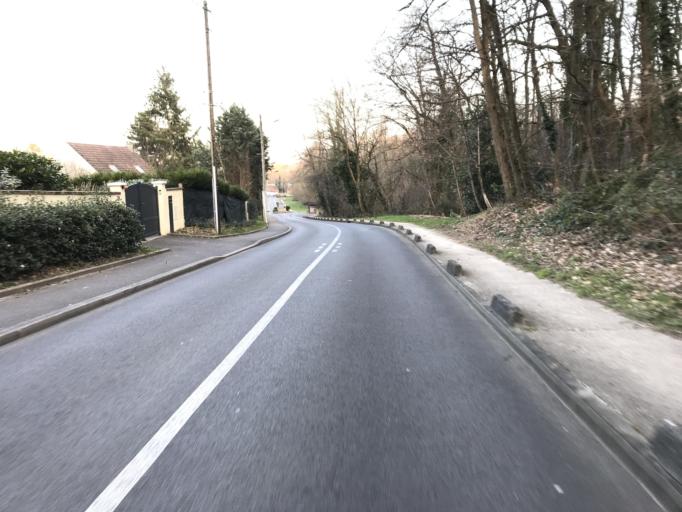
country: FR
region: Ile-de-France
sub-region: Departement de l'Essonne
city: Nozay
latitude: 48.6629
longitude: 2.2535
